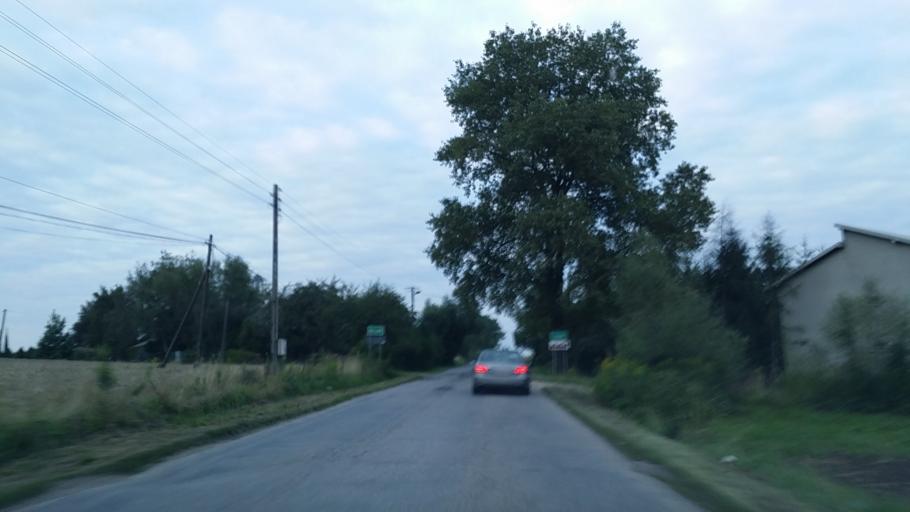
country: PL
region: Lesser Poland Voivodeship
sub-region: Powiat krakowski
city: Kaszow
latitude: 50.0266
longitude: 19.7395
